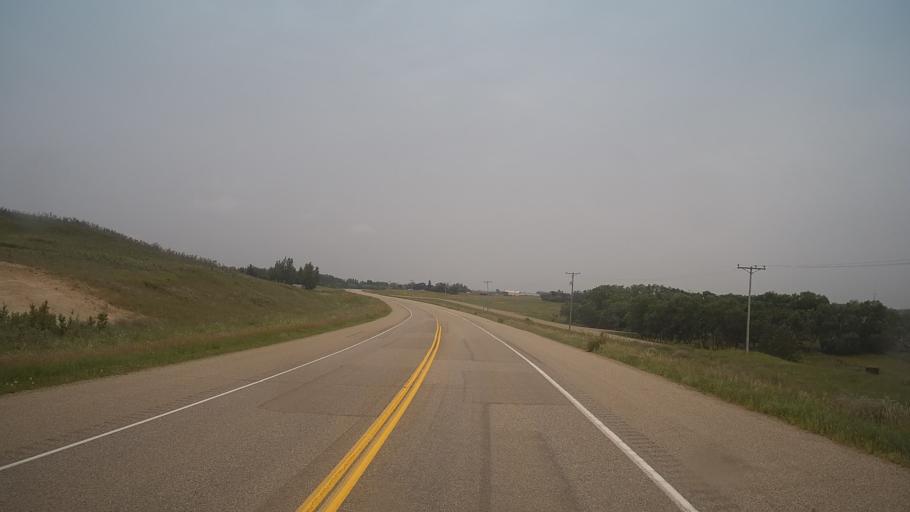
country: CA
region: Saskatchewan
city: Biggar
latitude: 52.0584
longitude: -107.8919
